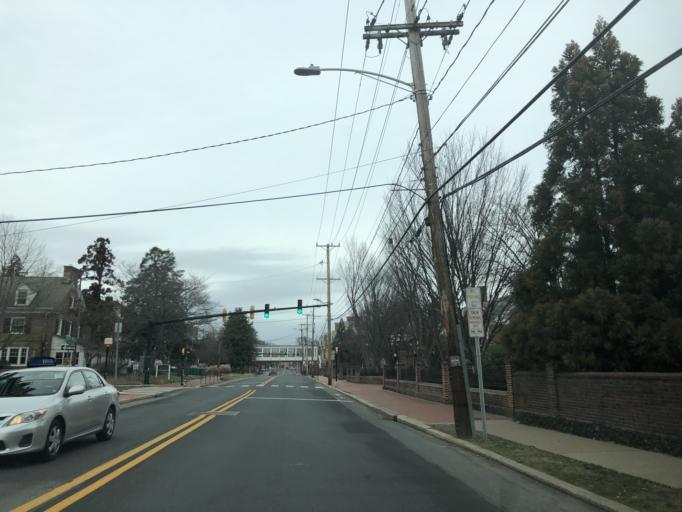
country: US
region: Delaware
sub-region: New Castle County
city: Newark
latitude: 39.6785
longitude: -75.7535
